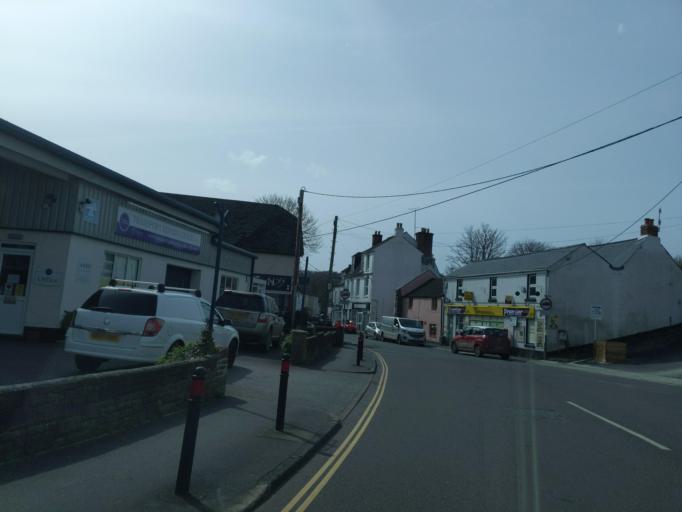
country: GB
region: England
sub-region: Devon
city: Plympton
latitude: 50.3937
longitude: -4.0537
